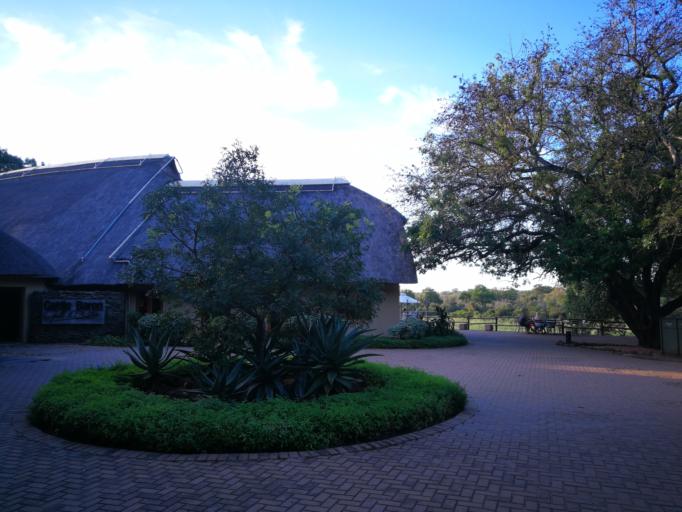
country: ZA
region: Limpopo
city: Thulamahashi
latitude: -24.9925
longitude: 31.5922
